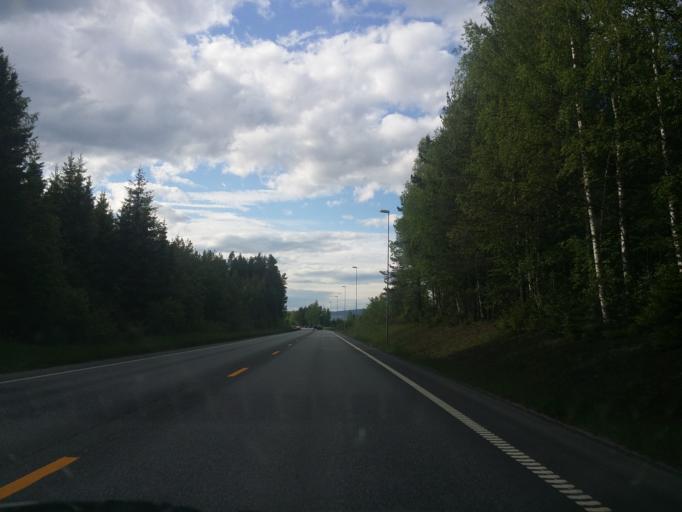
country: NO
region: Hedmark
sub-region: Stange
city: Stange
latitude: 60.7528
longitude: 11.1955
